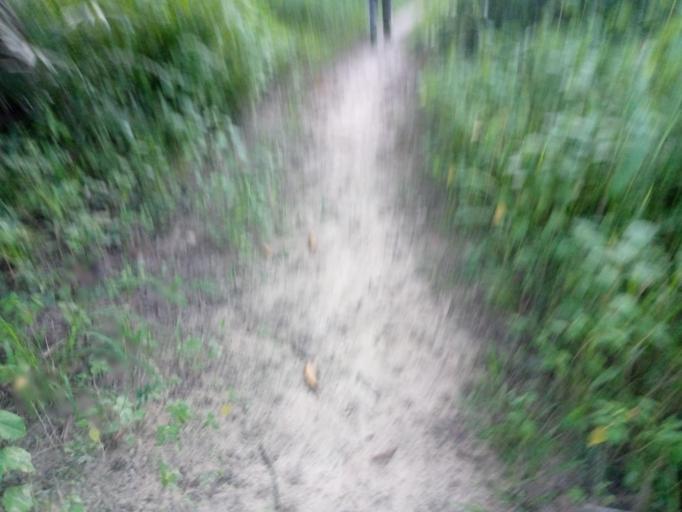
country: GM
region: Western
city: Gunjur
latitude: 13.0406
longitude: -16.7248
